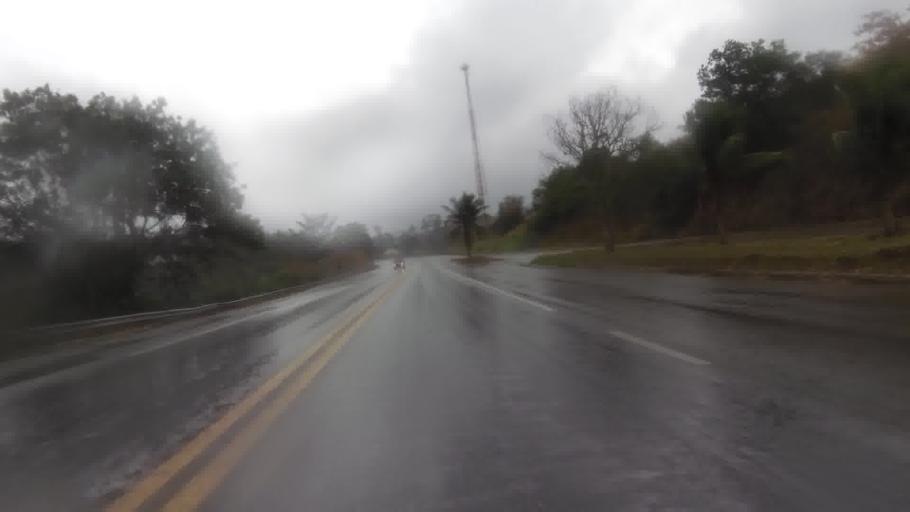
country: BR
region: Espirito Santo
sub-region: Cachoeiro De Itapemirim
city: Cachoeiro de Itapemirim
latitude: -20.9198
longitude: -41.0763
